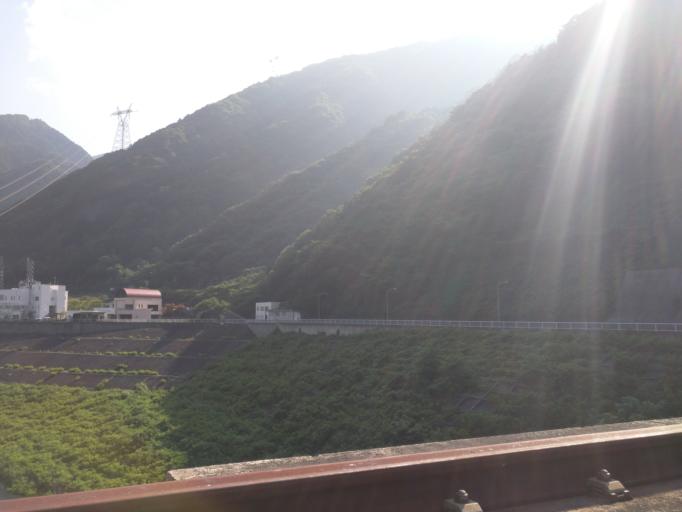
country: JP
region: Fukushima
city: Inawashiro
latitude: 37.3477
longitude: 139.9099
